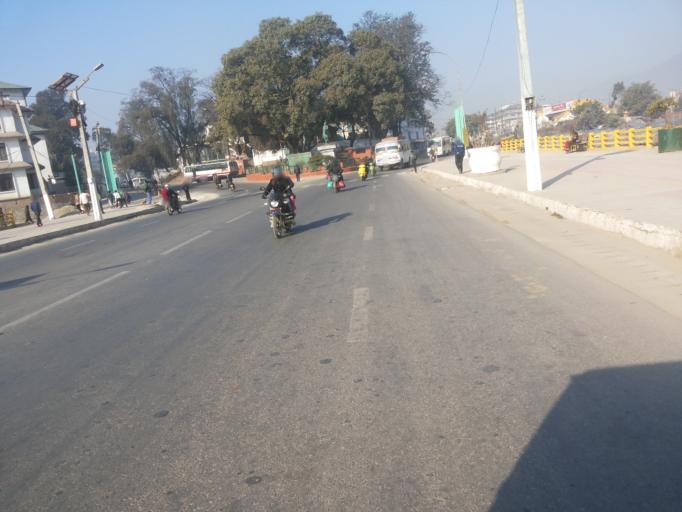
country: NP
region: Central Region
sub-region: Bagmati Zone
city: Kathmandu
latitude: 27.6992
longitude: 85.3181
